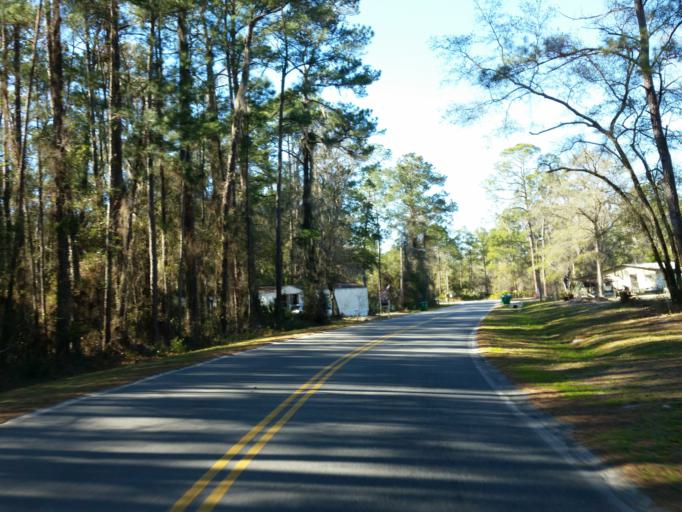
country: US
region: Florida
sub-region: Suwannee County
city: Wellborn
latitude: 30.3349
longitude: -82.7687
